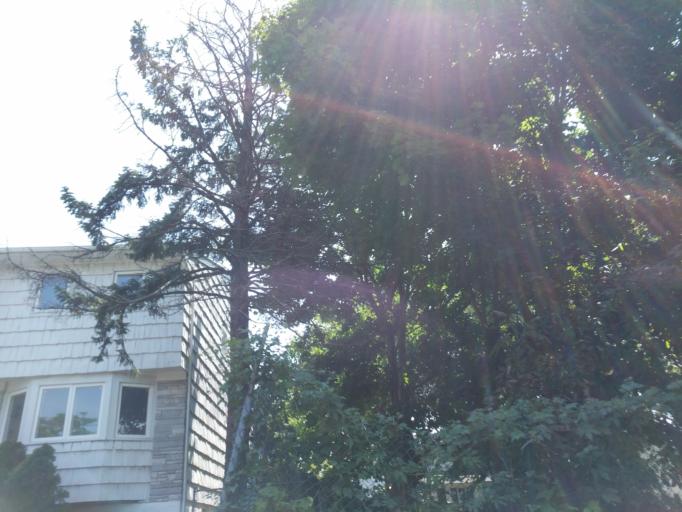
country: US
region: New York
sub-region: Nassau County
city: Cedarhurst
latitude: 40.6352
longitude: -73.7325
